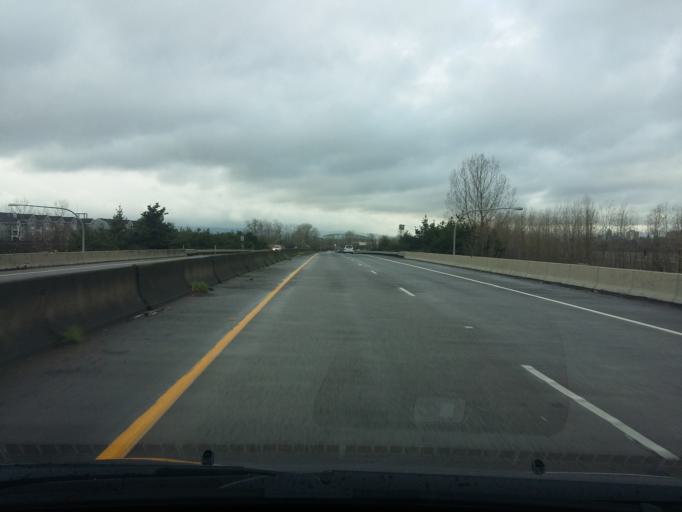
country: US
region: Washington
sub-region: Clark County
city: Vancouver
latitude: 45.6185
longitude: -122.6511
